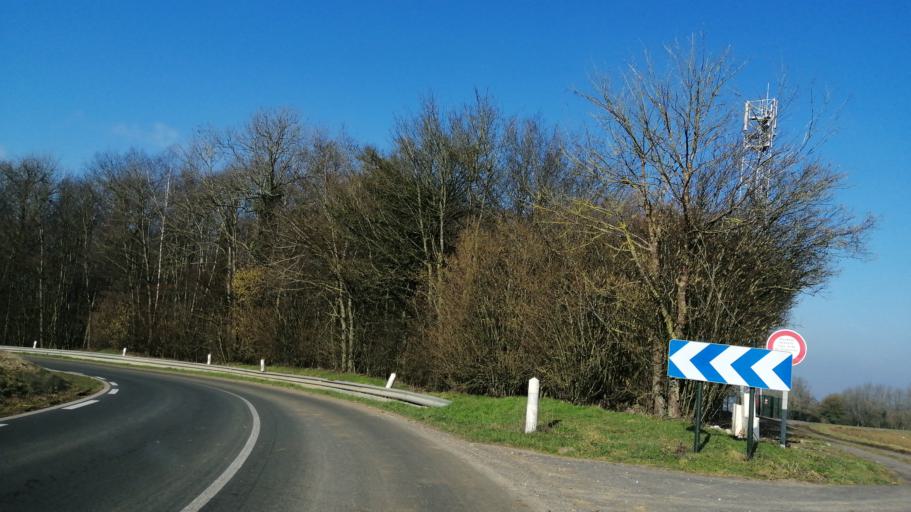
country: FR
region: Nord-Pas-de-Calais
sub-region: Departement du Pas-de-Calais
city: Ranchicourt
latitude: 50.4098
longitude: 2.5896
